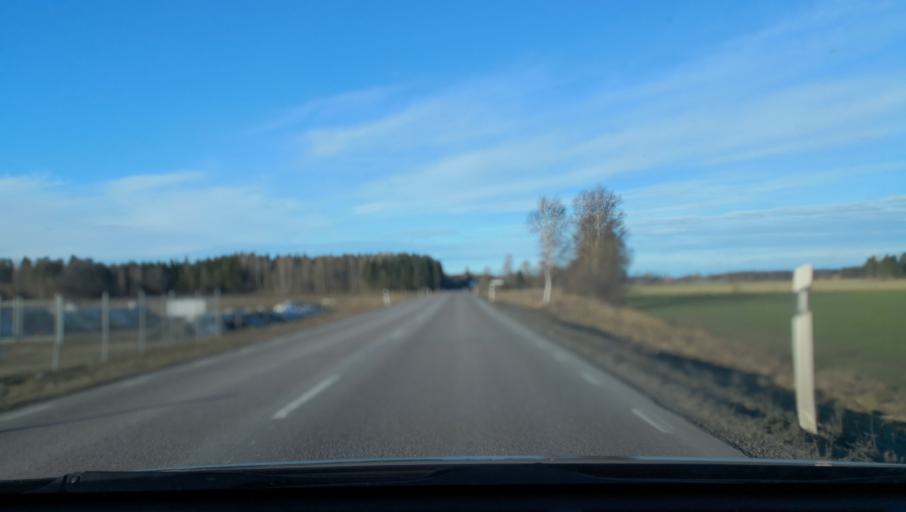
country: SE
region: Uppsala
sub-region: Osthammars Kommun
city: Gimo
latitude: 60.1822
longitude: 18.1904
